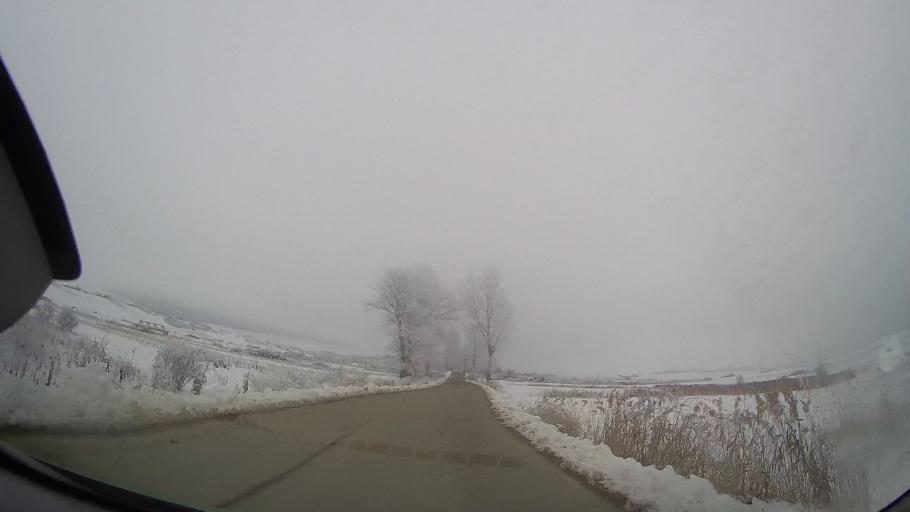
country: RO
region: Iasi
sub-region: Comuna Tansa
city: Tansa
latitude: 46.9121
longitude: 27.2136
